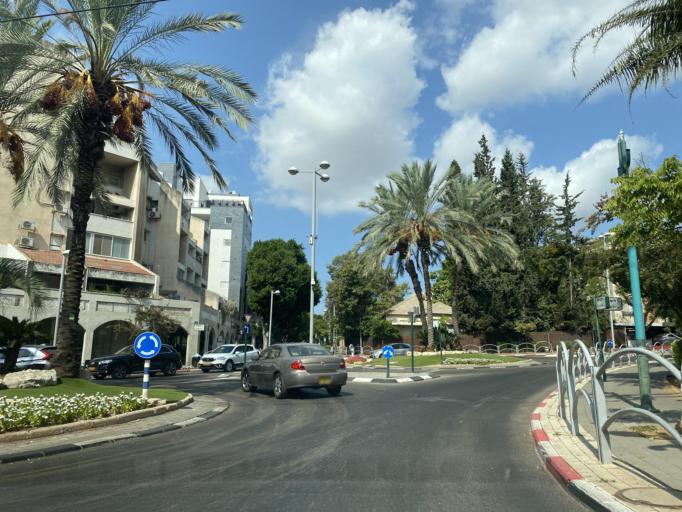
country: IL
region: Central District
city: Kfar Saba
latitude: 32.1780
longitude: 34.9096
